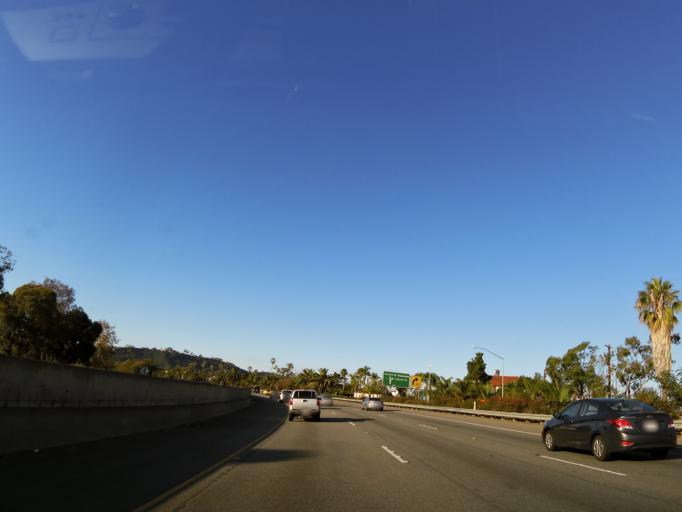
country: US
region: California
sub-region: Santa Barbara County
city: Santa Barbara
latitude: 34.4196
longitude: -119.6867
